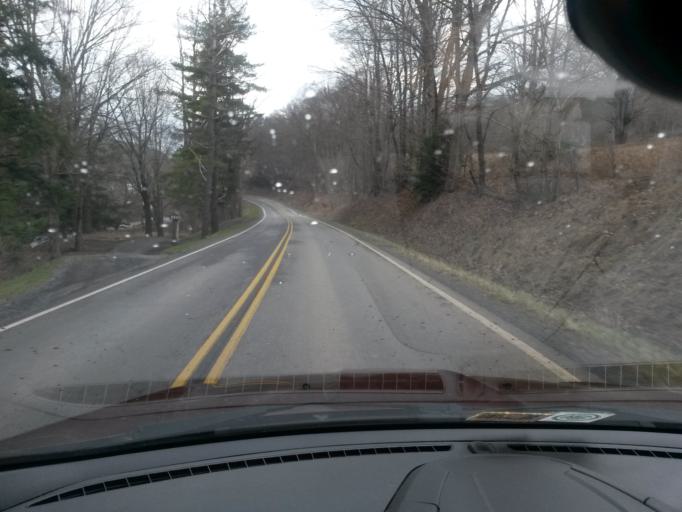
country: US
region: Virginia
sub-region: Highland County
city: Monterey
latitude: 38.3627
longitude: -79.6302
